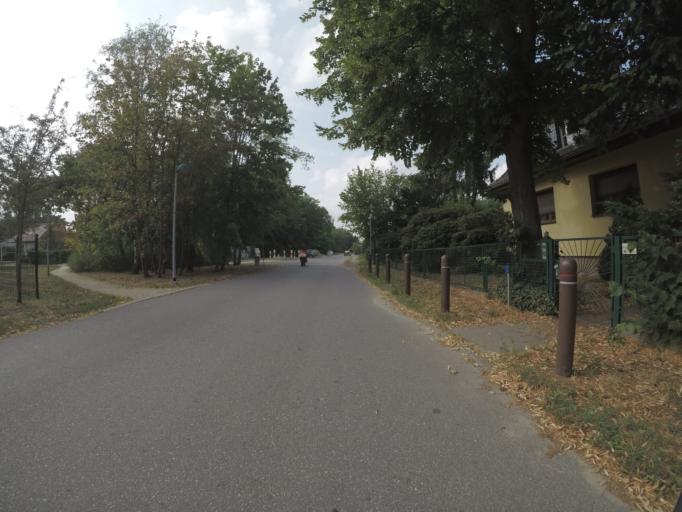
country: DE
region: Brandenburg
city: Rangsdorf
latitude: 52.3455
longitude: 13.4230
